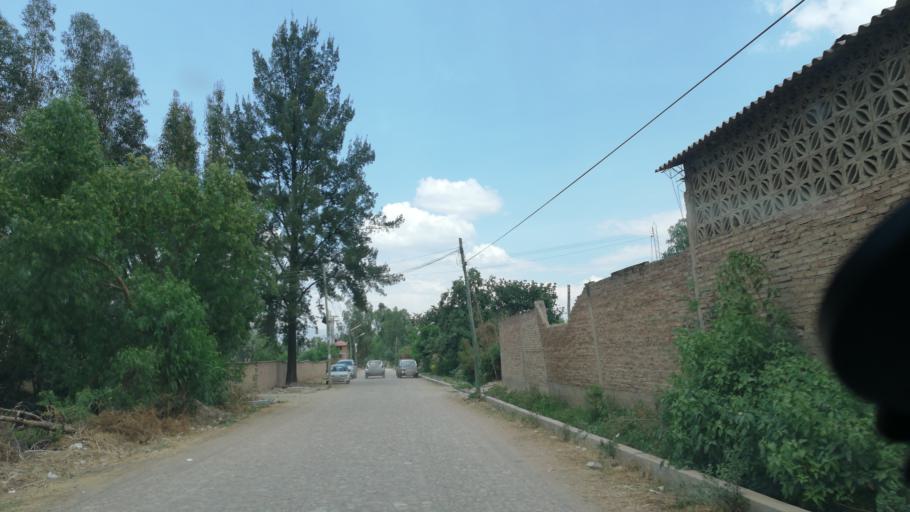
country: BO
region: Cochabamba
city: Cochabamba
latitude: -17.3575
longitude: -66.2212
